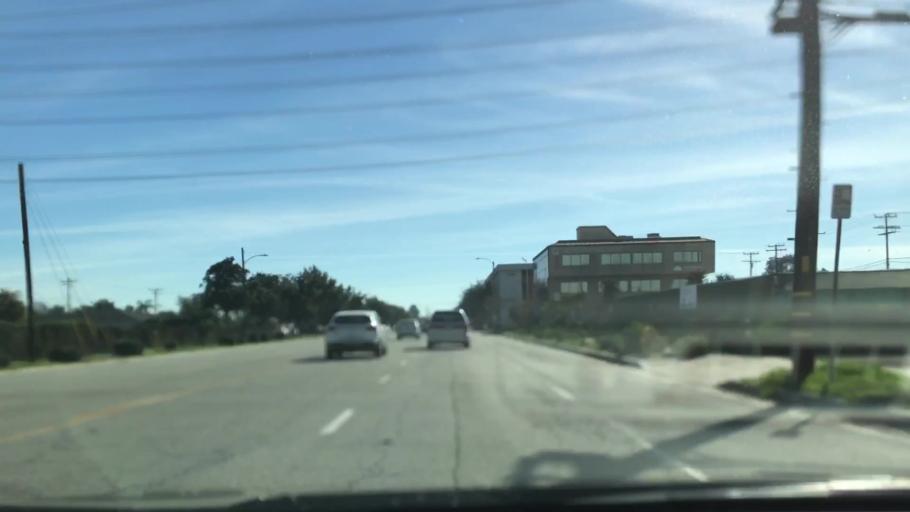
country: US
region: California
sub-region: Los Angeles County
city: Alondra Park
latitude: 33.8711
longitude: -118.3266
